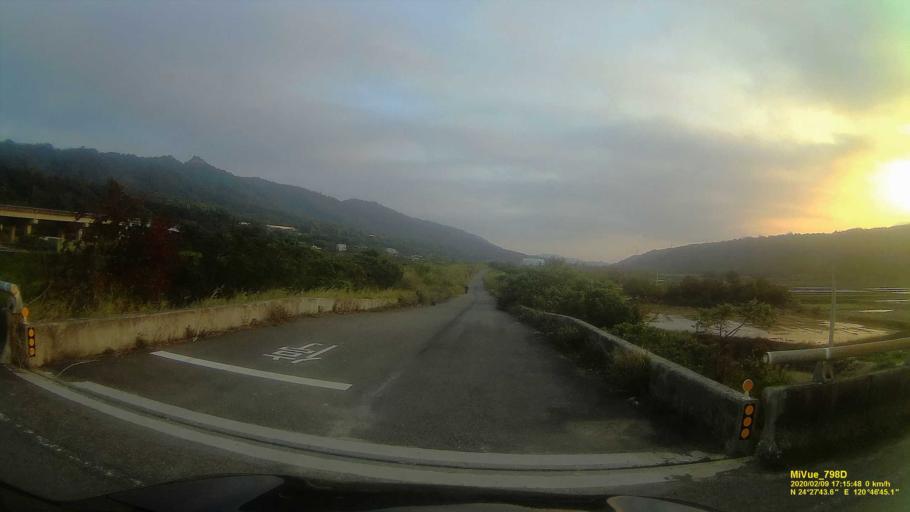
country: TW
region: Taiwan
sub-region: Miaoli
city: Miaoli
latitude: 24.4620
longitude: 120.7790
